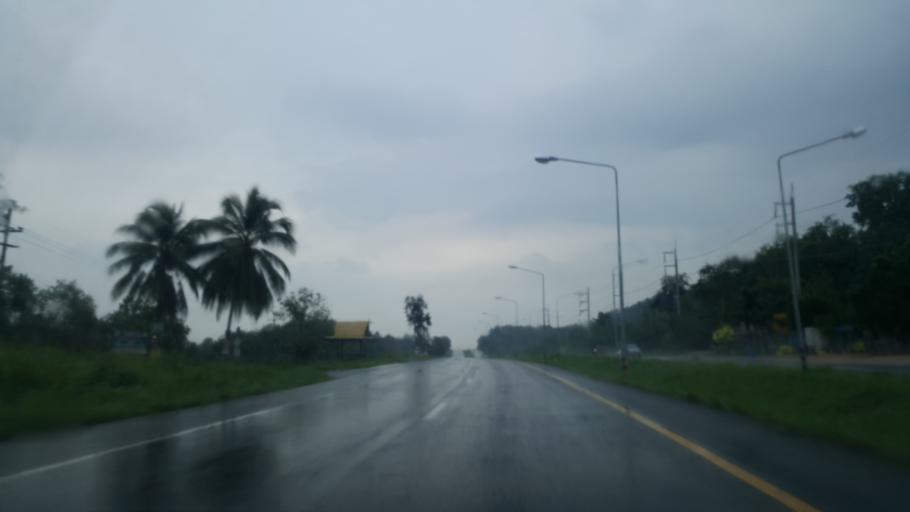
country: TH
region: Chon Buri
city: Ban Talat Bueng
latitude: 12.9935
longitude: 101.0616
